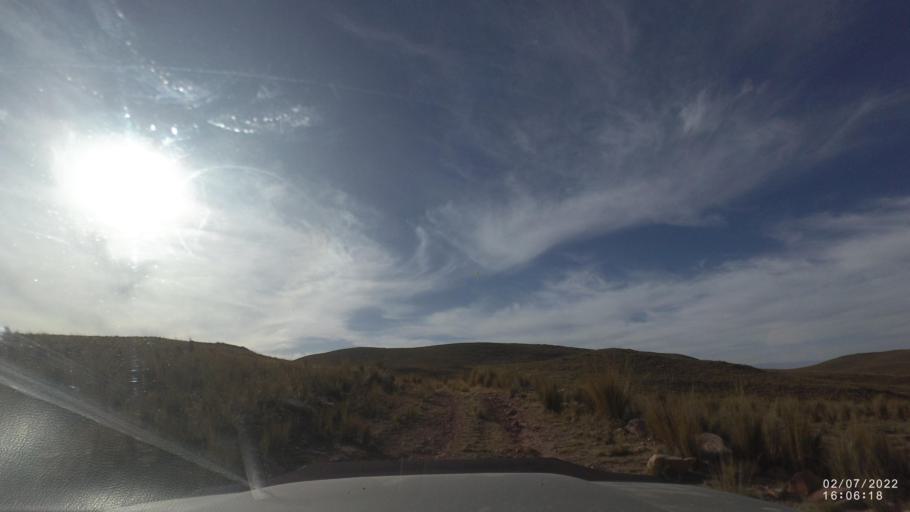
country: BO
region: Cochabamba
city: Irpa Irpa
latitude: -17.9112
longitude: -66.4433
